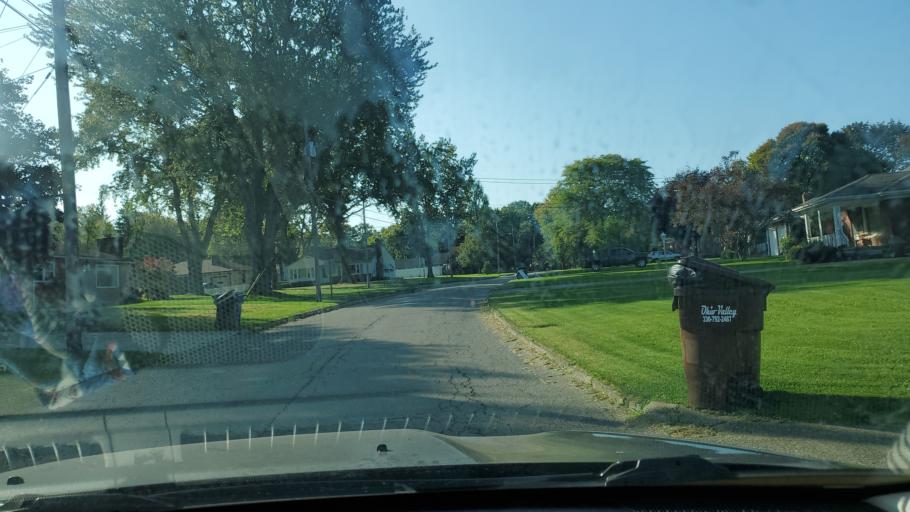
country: US
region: Ohio
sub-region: Mahoning County
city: Boardman
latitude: 41.0484
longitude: -80.6503
